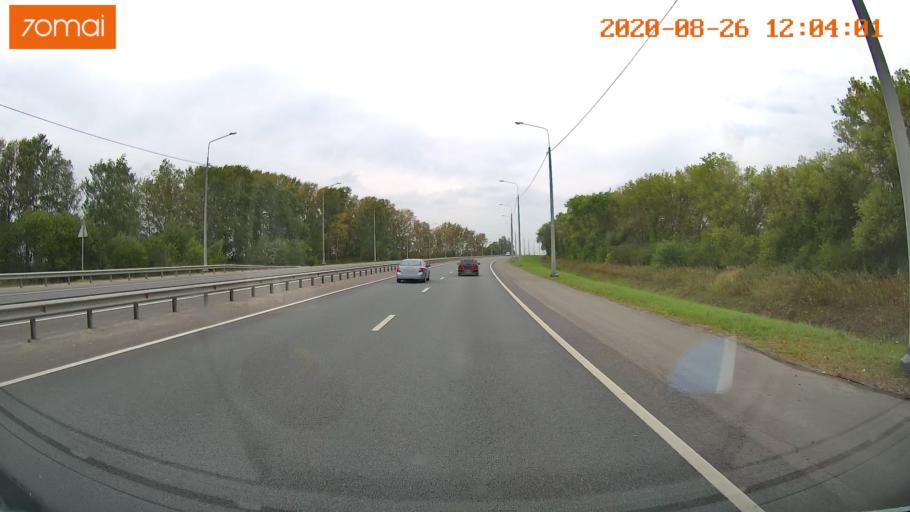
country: RU
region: Rjazan
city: Kiritsy
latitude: 54.3054
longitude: 40.1959
